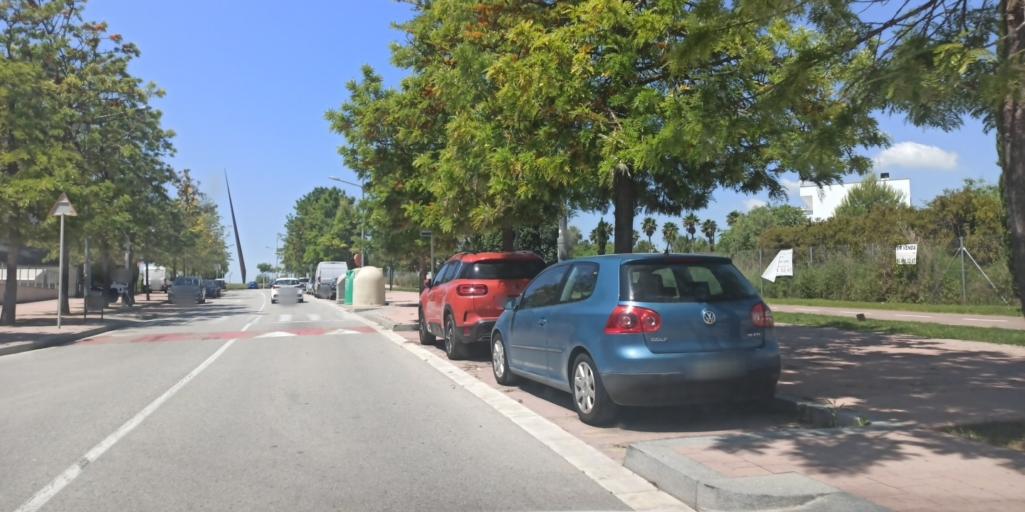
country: ES
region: Catalonia
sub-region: Provincia de Barcelona
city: Sitges
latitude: 41.2416
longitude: 1.8008
